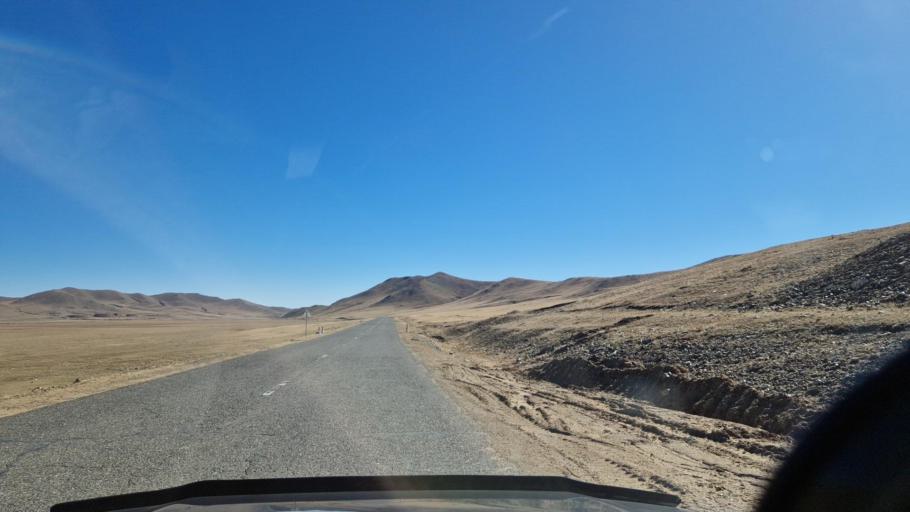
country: MN
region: Hentiy
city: Modot
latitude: 47.6917
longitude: 109.0907
